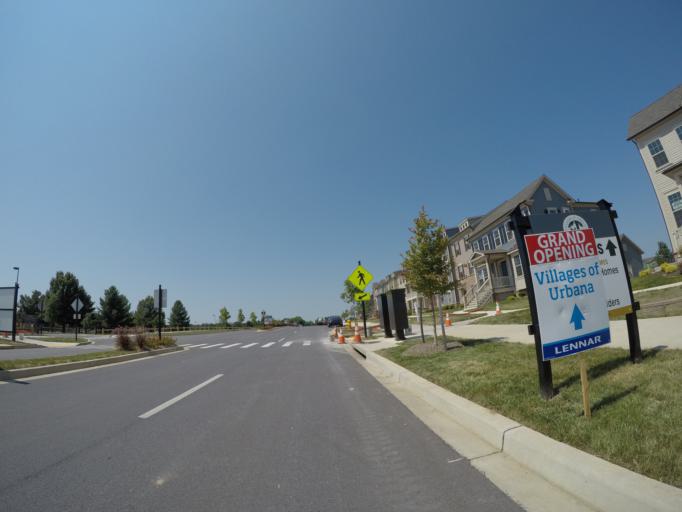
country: US
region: Maryland
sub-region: Frederick County
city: Urbana
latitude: 39.3294
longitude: -77.3611
